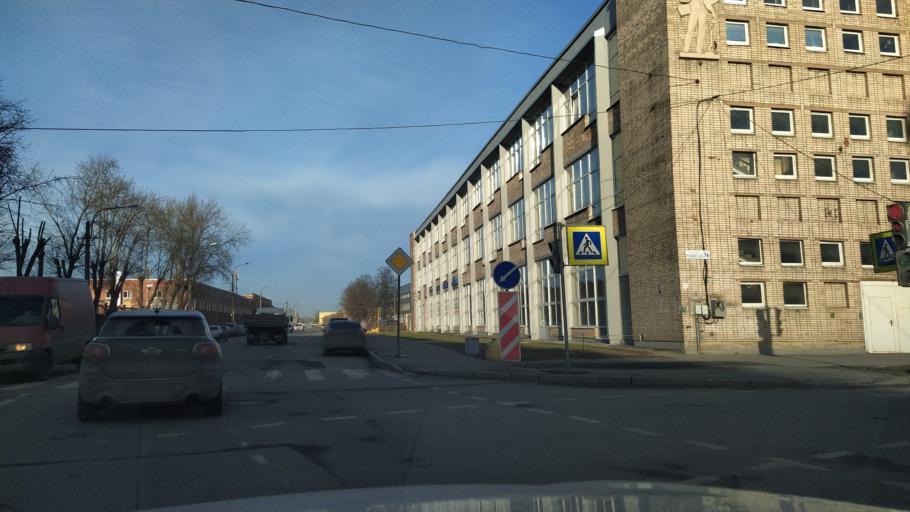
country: RU
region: St.-Petersburg
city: Kupchino
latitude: 59.8815
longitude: 30.3381
